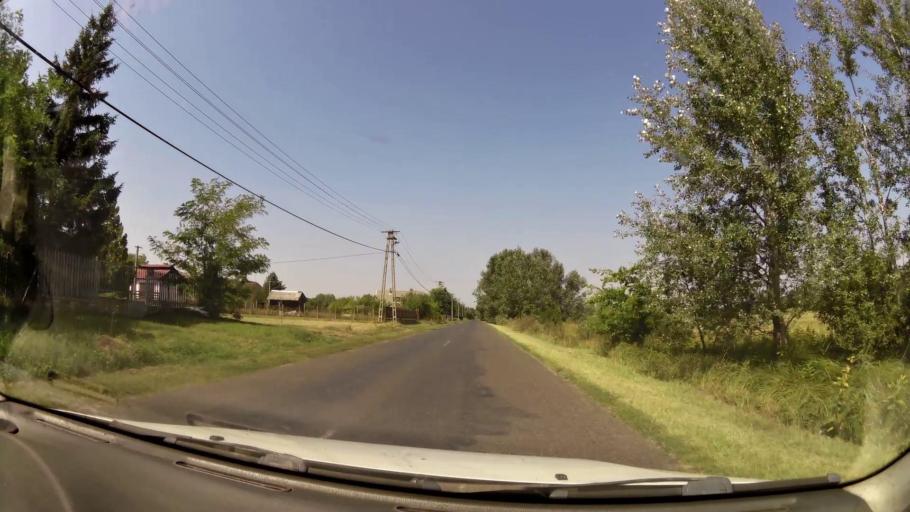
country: HU
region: Pest
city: Tapioszentmarton
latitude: 47.3393
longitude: 19.7911
